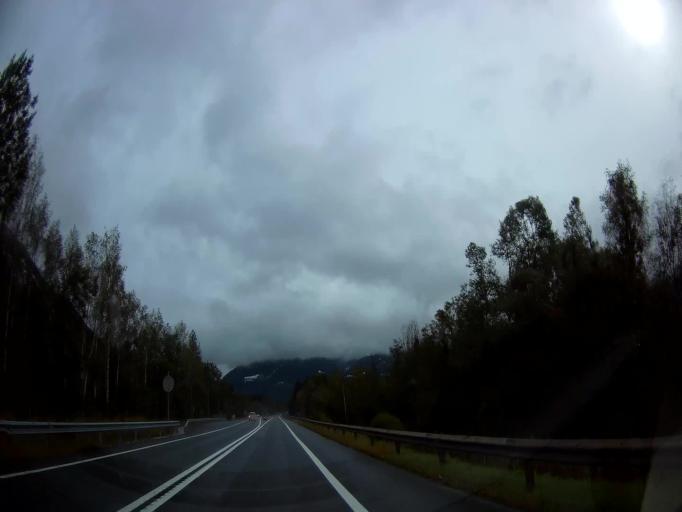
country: AT
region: Styria
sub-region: Politischer Bezirk Liezen
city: Lassing
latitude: 47.5572
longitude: 14.2743
